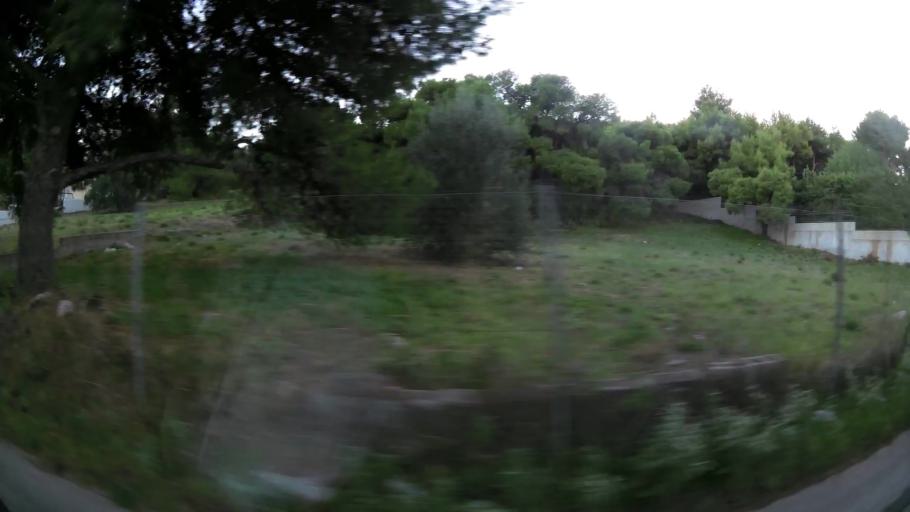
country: GR
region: Attica
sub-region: Nomarchia Anatolikis Attikis
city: Vouliagmeni
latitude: 37.8215
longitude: 23.7924
